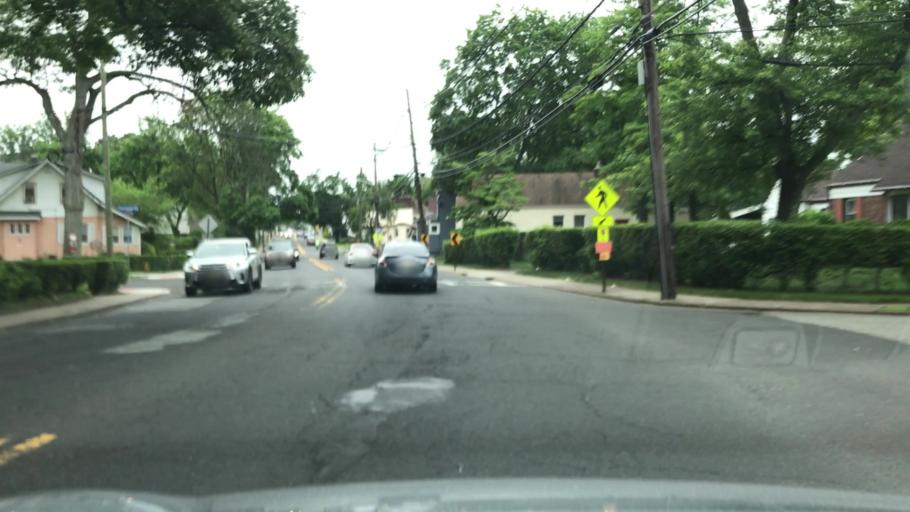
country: US
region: New Jersey
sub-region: Bergen County
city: Bergenfield
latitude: 40.9081
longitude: -73.9988
